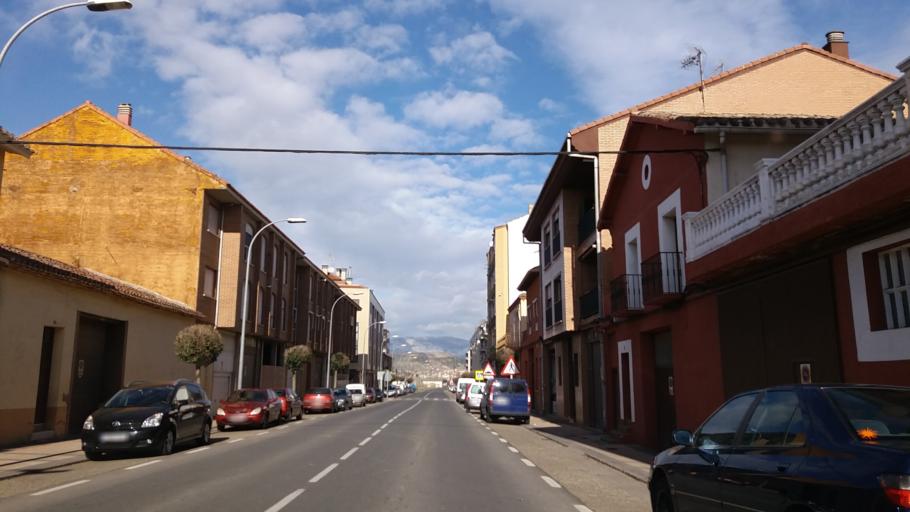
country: ES
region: La Rioja
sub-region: Provincia de La Rioja
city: Fuenmayor
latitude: 42.4687
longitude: -2.5609
